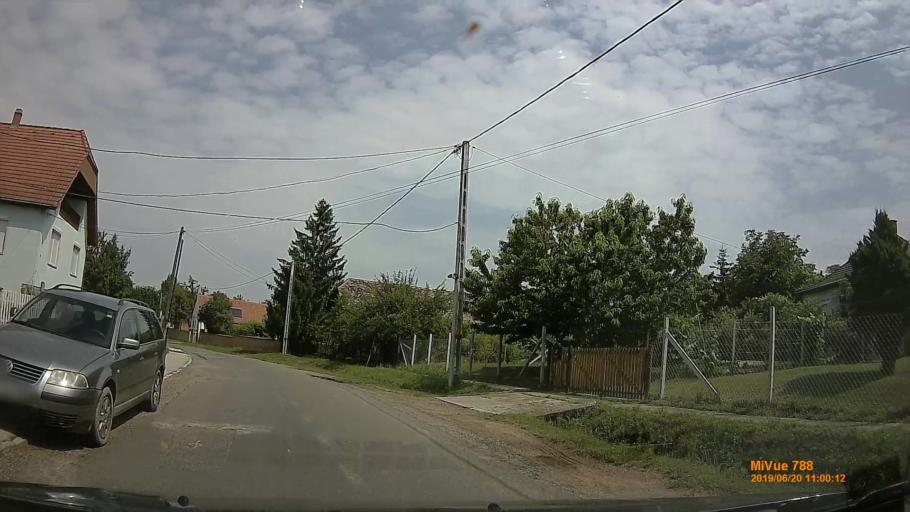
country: HU
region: Baranya
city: Mecseknadasd
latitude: 46.1711
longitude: 18.5130
